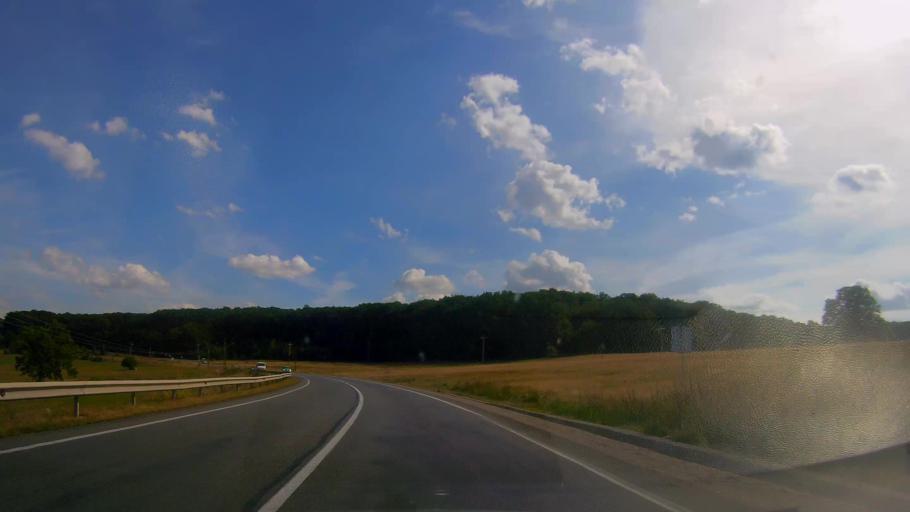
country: RO
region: Brasov
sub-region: Oras Rupea
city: Fiser
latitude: 46.0907
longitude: 25.1180
